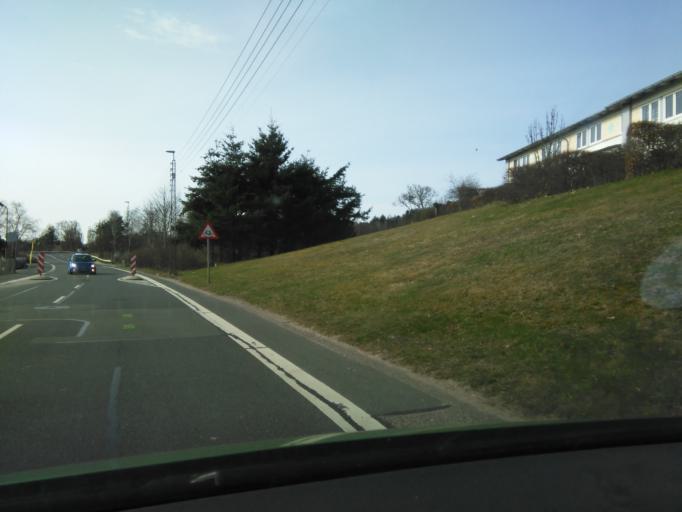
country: DK
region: Central Jutland
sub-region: Silkeborg Kommune
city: Silkeborg
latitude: 56.1872
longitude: 9.5441
